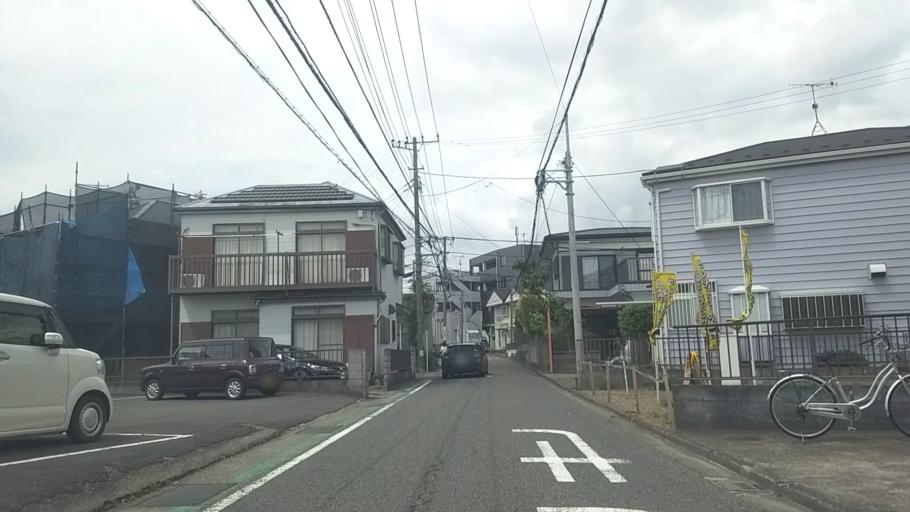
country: JP
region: Kanagawa
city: Fujisawa
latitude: 35.3457
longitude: 139.4556
